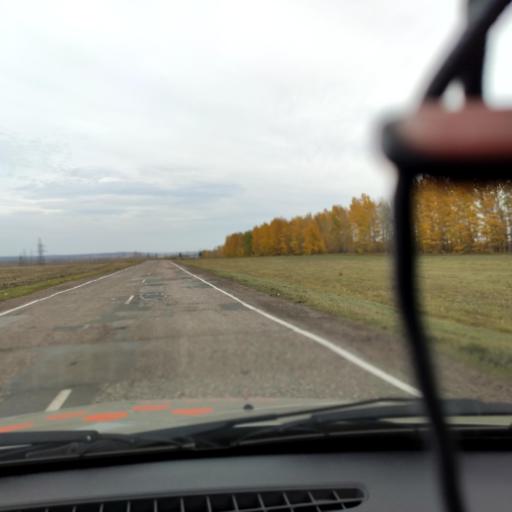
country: RU
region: Bashkortostan
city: Kabakovo
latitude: 54.5231
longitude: 56.0508
